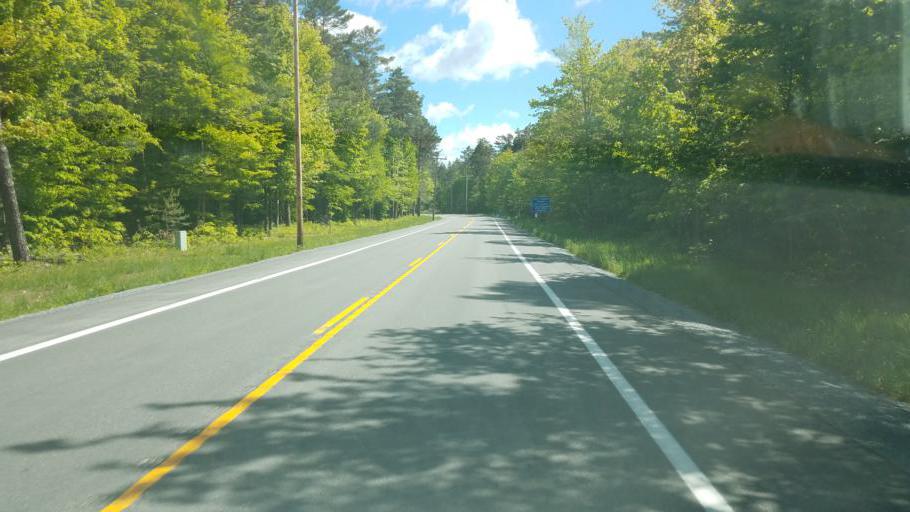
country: US
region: New York
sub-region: Oneida County
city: Boonville
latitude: 43.4814
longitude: -75.1625
